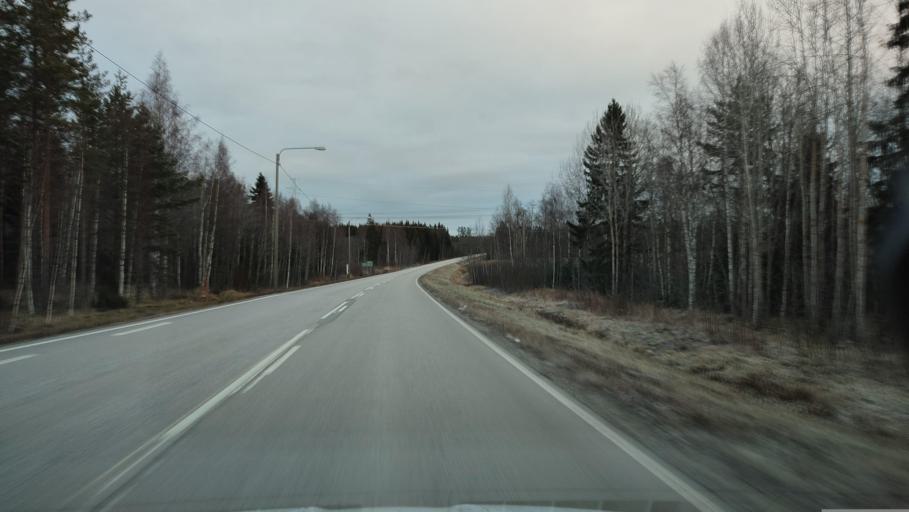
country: FI
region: Ostrobothnia
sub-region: Sydosterbotten
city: Kristinestad
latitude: 62.2960
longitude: 21.3851
